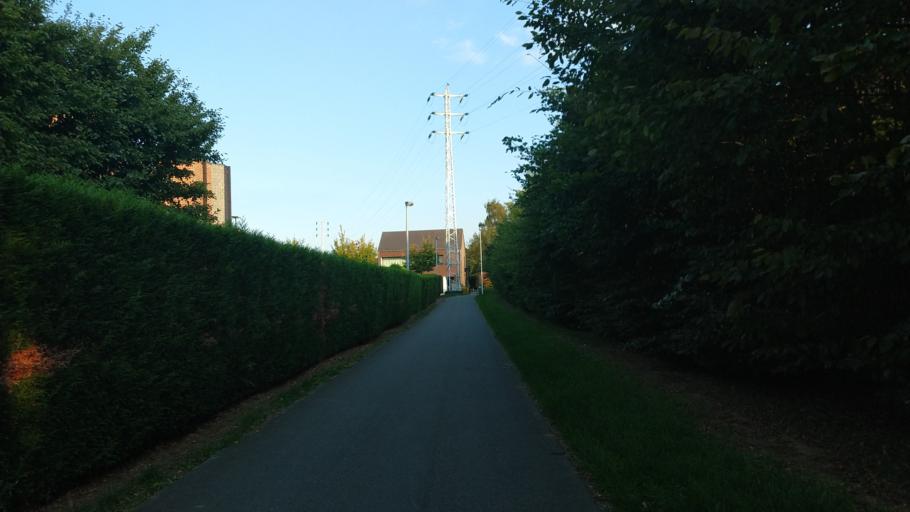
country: BE
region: Flanders
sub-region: Provincie Vlaams-Brabant
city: Holsbeek
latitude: 50.8853
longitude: 4.7488
